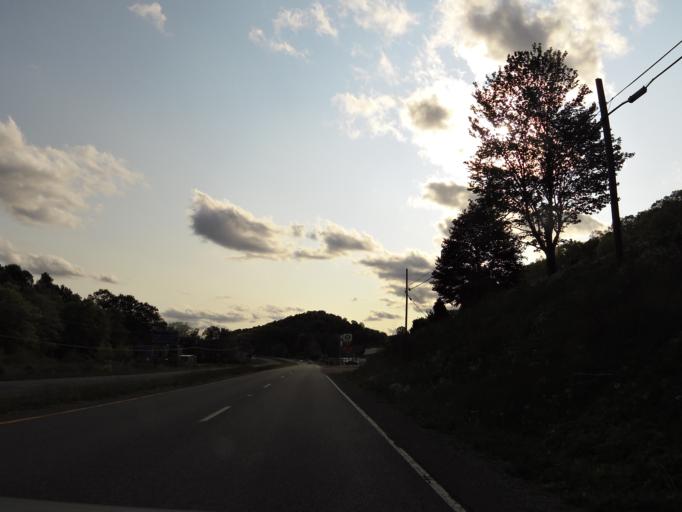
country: US
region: Virginia
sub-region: Tazewell County
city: Springville
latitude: 37.1969
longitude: -81.3985
